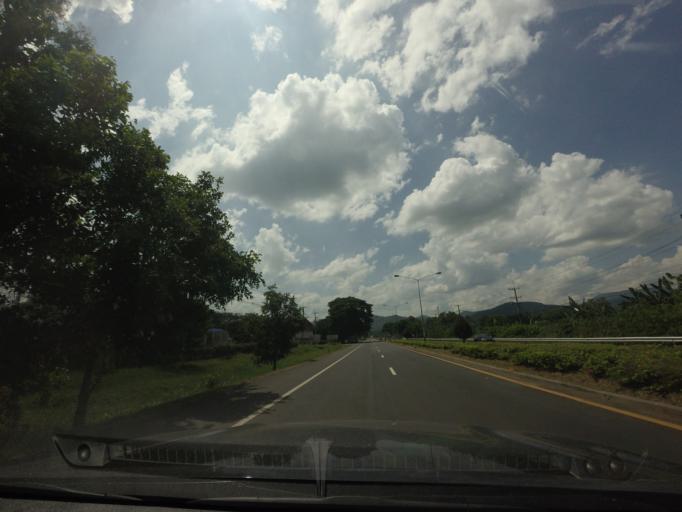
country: TH
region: Phetchabun
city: Phetchabun
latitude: 16.2666
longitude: 101.0529
